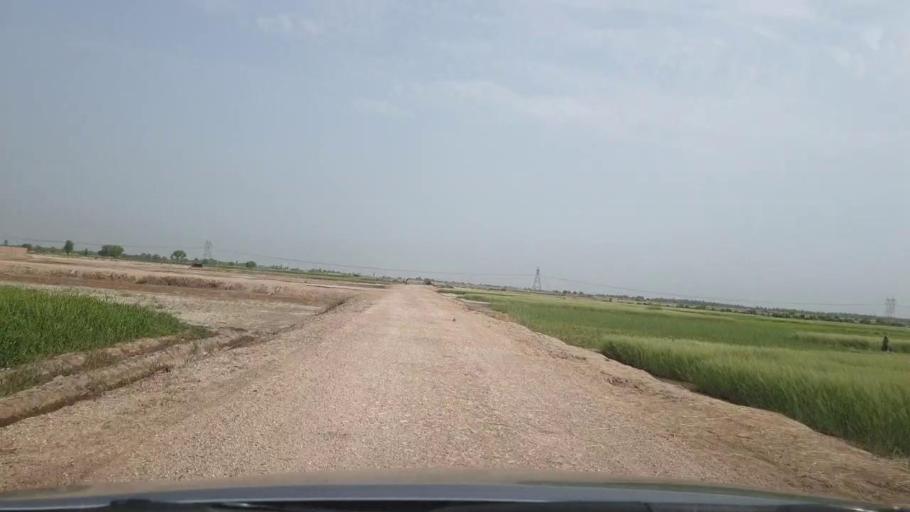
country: PK
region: Sindh
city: Rohri
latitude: 27.6665
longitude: 69.0259
